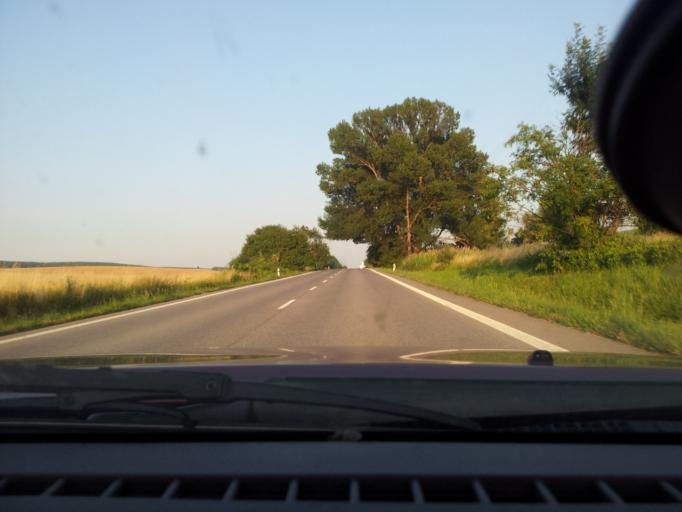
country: SK
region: Trnavsky
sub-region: Okres Senica
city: Senica
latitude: 48.7481
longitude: 17.3333
